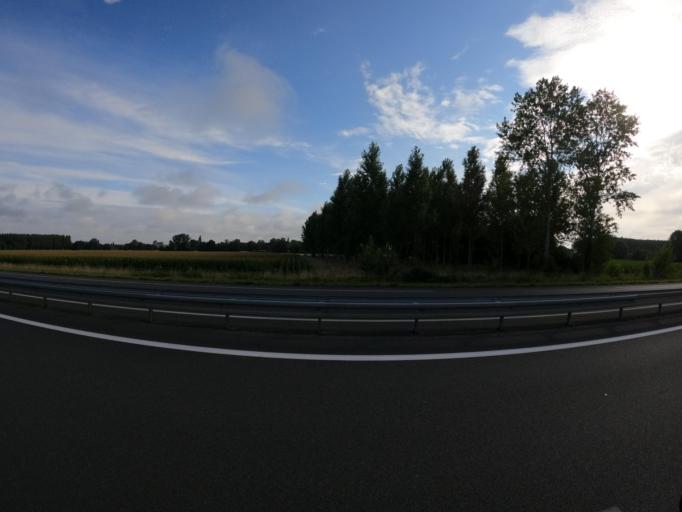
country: FR
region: Pays de la Loire
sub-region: Departement de Maine-et-Loire
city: Villebernier
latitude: 47.2939
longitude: -0.0205
